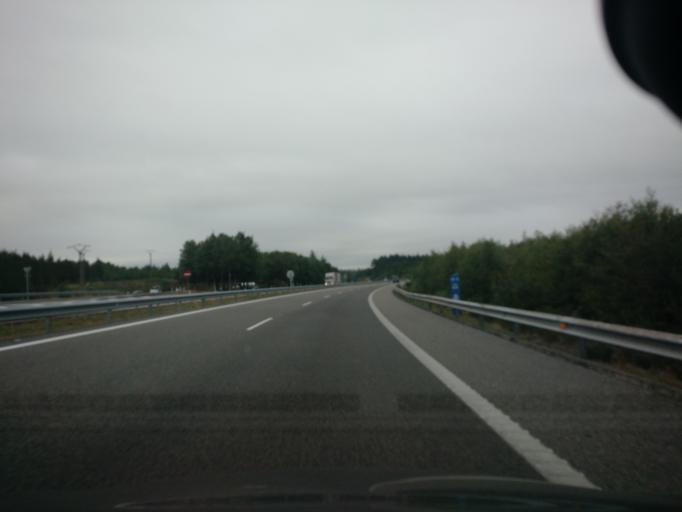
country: ES
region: Galicia
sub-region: Provincia da Coruna
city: Oroso
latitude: 42.9406
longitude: -8.4621
